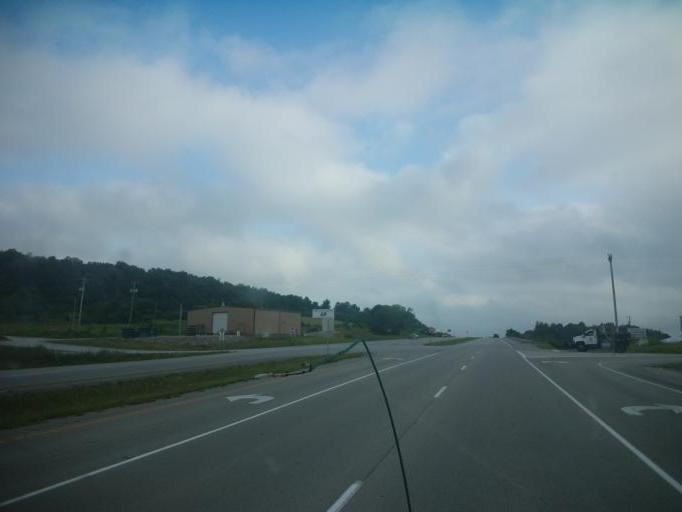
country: US
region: Kentucky
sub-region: Clinton County
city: Albany
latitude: 36.7406
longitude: -85.1345
